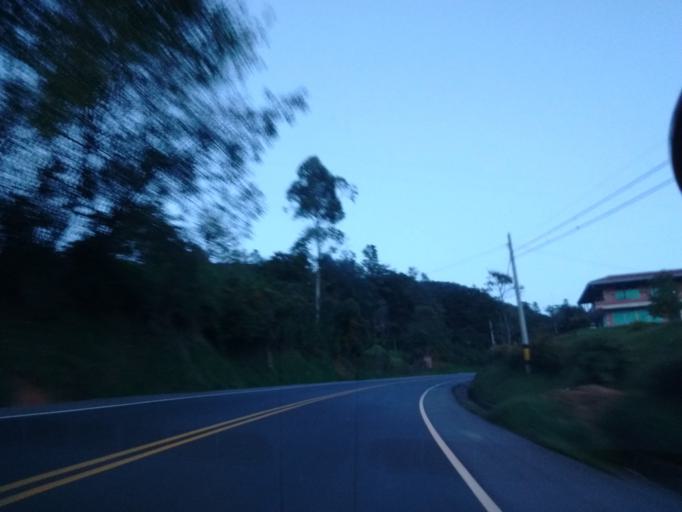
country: CO
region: Antioquia
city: Santuario
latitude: 6.1236
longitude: -75.2378
